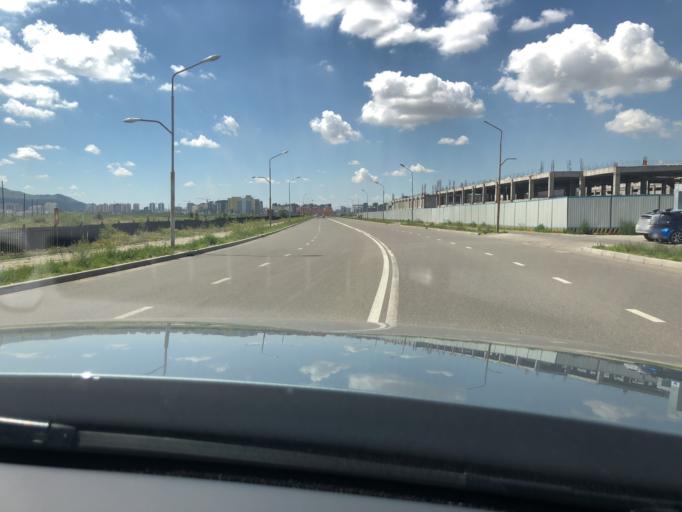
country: MN
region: Ulaanbaatar
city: Ulaanbaatar
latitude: 47.9051
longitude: 106.9718
